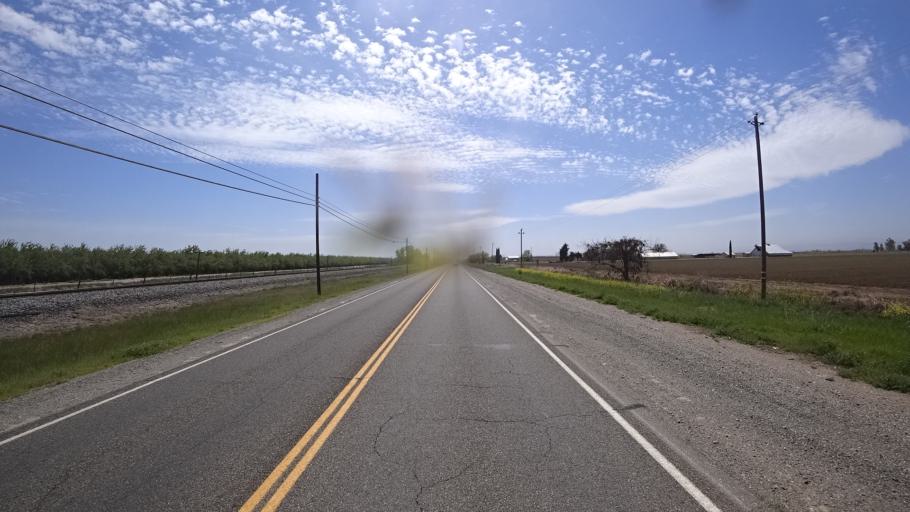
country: US
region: California
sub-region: Glenn County
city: Willows
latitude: 39.5727
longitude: -122.1938
